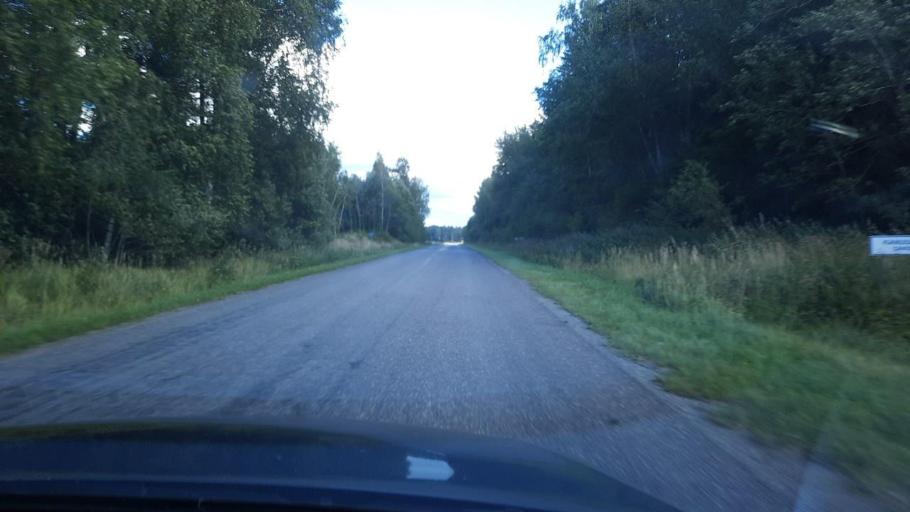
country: EE
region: Paernumaa
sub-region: Tootsi vald
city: Tootsi
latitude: 58.4902
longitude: 24.9387
